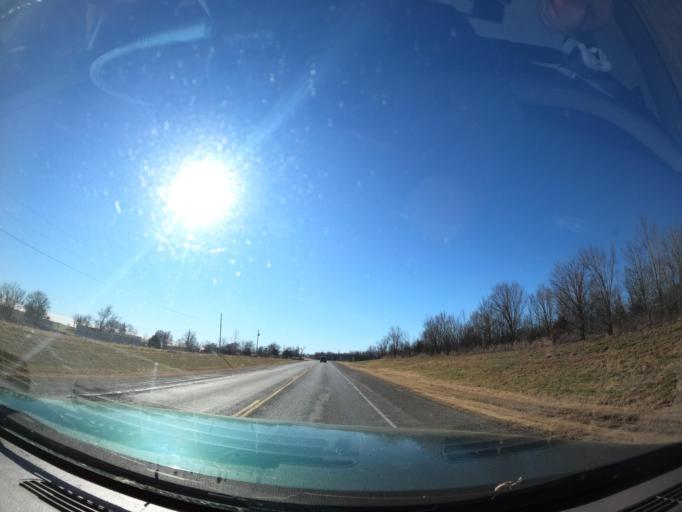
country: US
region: Oklahoma
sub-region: Muskogee County
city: Haskell
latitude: 35.8692
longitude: -95.6715
